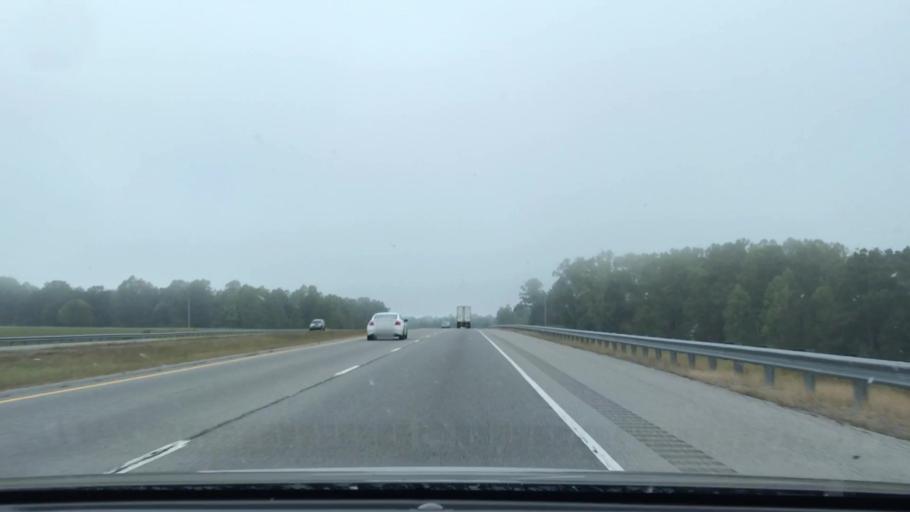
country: US
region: Tennessee
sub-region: Sumner County
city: Gallatin
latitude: 36.4770
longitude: -86.4764
